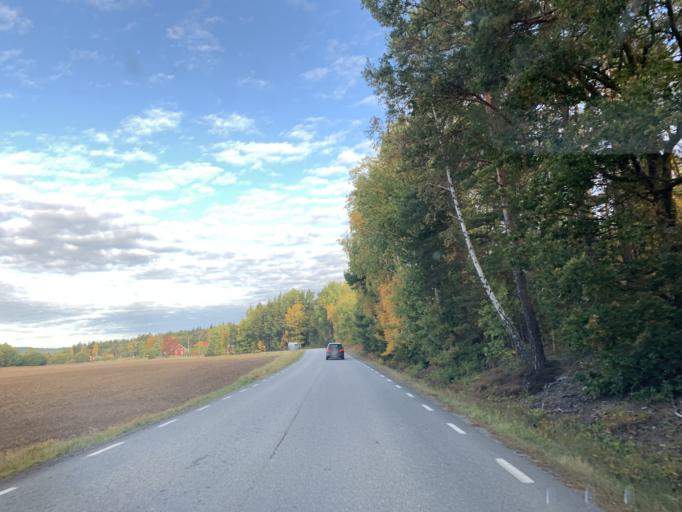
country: SE
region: Stockholm
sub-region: Upplands-Bro Kommun
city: Bro
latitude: 59.5065
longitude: 17.6047
